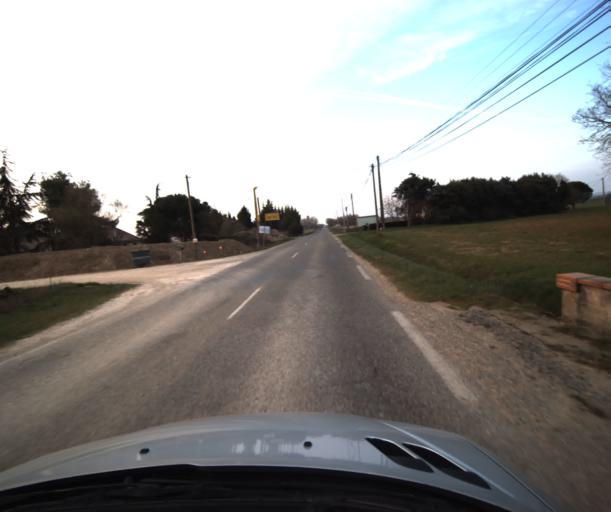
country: FR
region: Midi-Pyrenees
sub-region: Departement de la Haute-Garonne
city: Fronton
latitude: 43.8541
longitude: 1.3855
